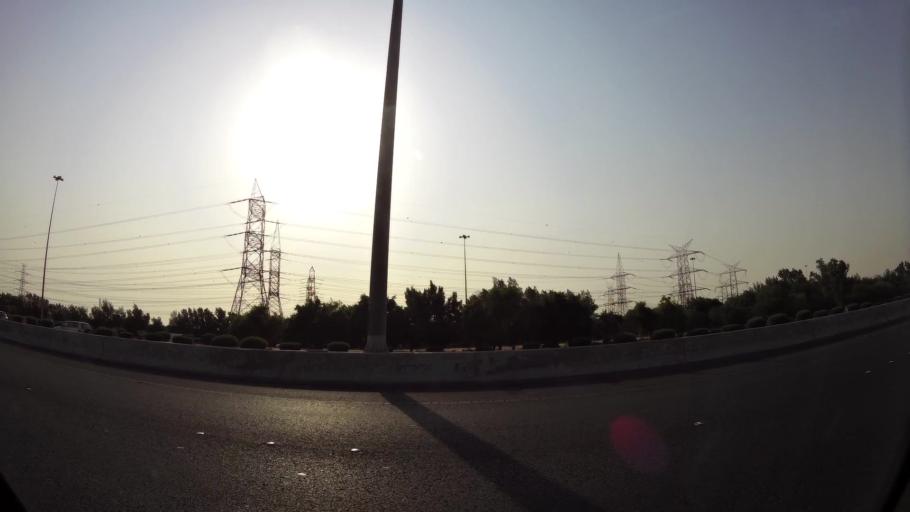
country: KW
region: Mubarak al Kabir
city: Sabah as Salim
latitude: 29.2622
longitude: 48.0434
